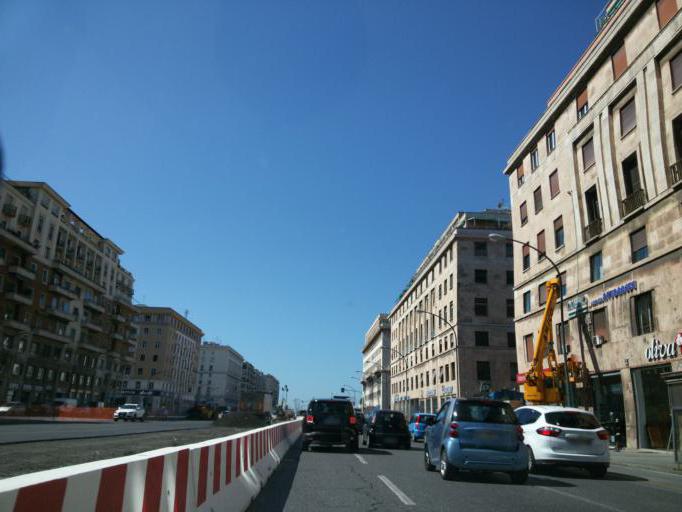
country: IT
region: Liguria
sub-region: Provincia di Genova
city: San Teodoro
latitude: 44.4032
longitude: 8.9466
